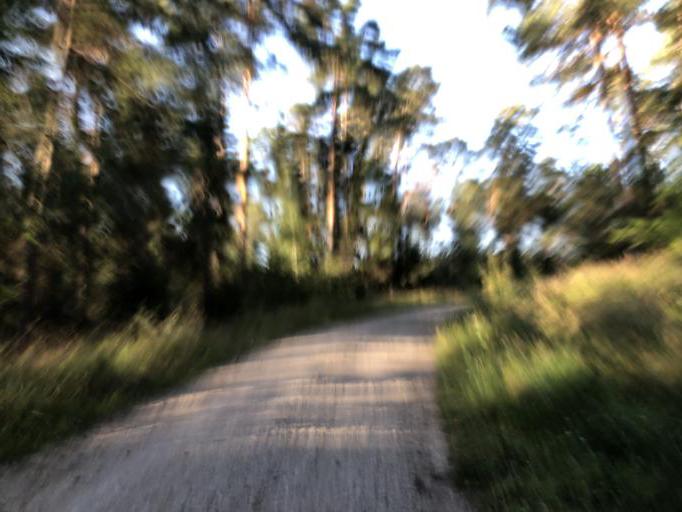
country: DE
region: Bavaria
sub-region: Regierungsbezirk Mittelfranken
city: Uttenreuth
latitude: 49.5639
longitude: 11.0846
